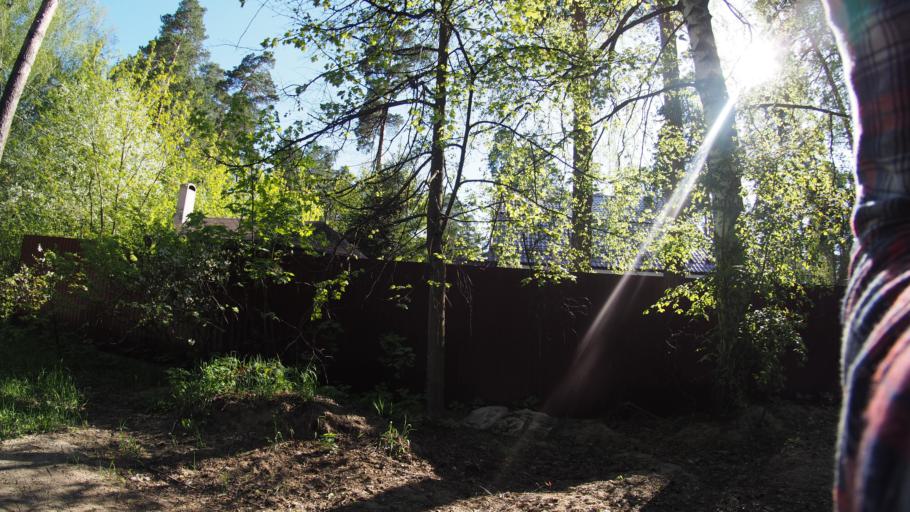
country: RU
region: Moskovskaya
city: Kratovo
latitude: 55.5768
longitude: 38.1828
